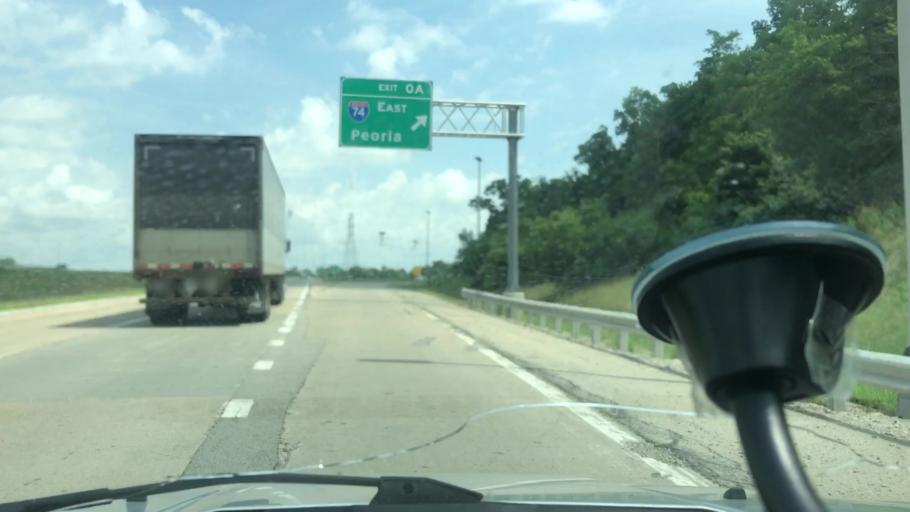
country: US
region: Illinois
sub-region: Peoria County
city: Bellevue
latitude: 40.7365
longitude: -89.6700
